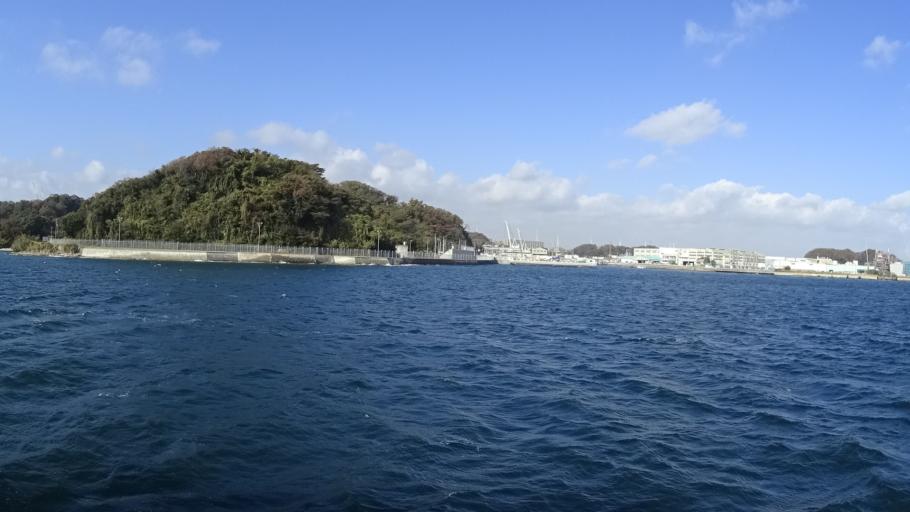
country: JP
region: Kanagawa
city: Yokosuka
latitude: 35.3035
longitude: 139.6442
